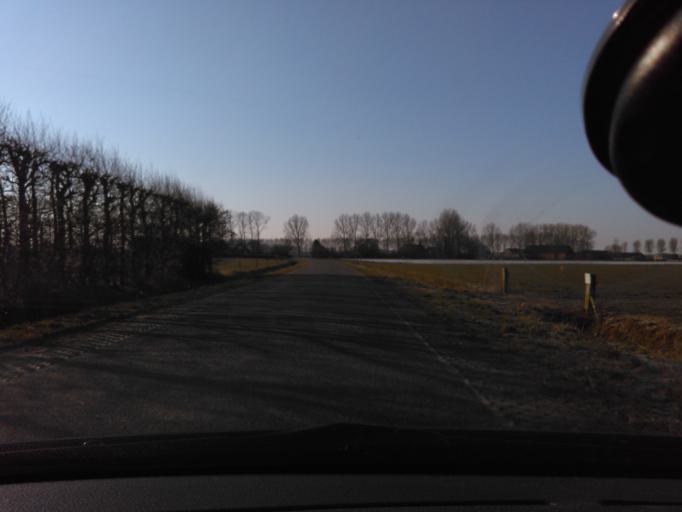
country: NL
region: Zeeland
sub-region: Gemeente Terneuzen
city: Koewacht
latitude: 51.2531
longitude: 3.9823
